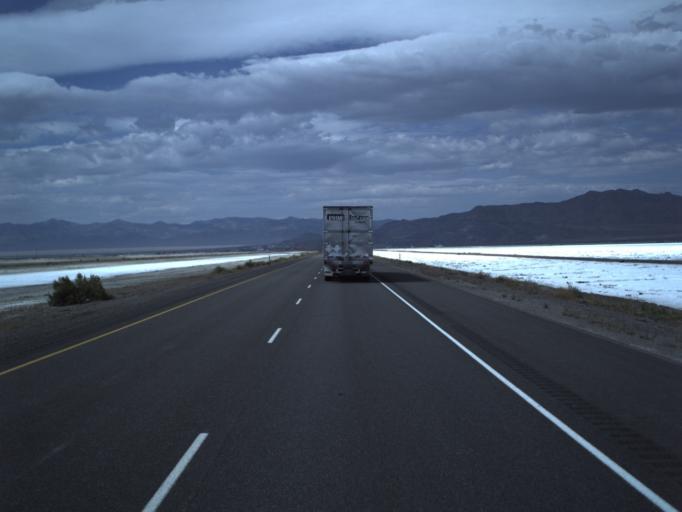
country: US
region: Utah
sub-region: Tooele County
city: Wendover
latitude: 40.7408
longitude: -113.9207
